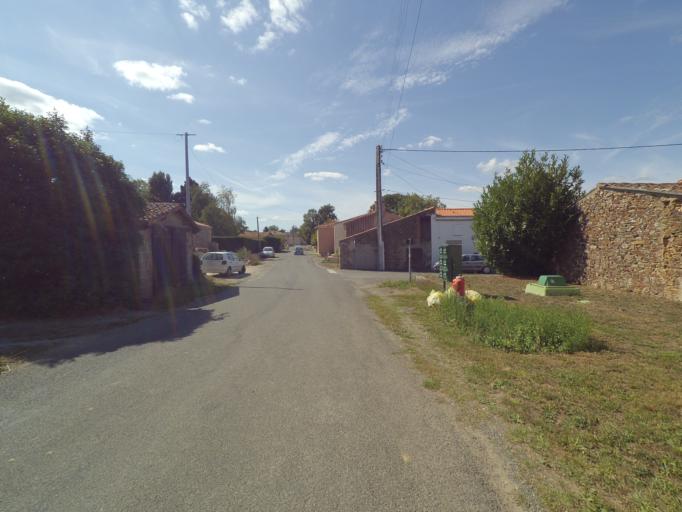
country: FR
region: Pays de la Loire
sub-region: Departement de la Loire-Atlantique
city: Vieillevigne
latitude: 46.9624
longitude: -1.4212
